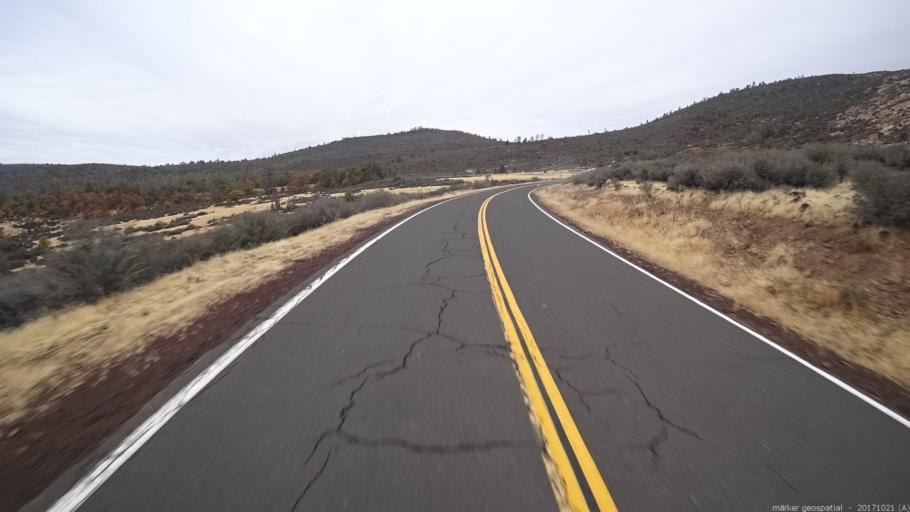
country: US
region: California
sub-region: Shasta County
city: Burney
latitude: 40.9991
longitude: -121.5043
